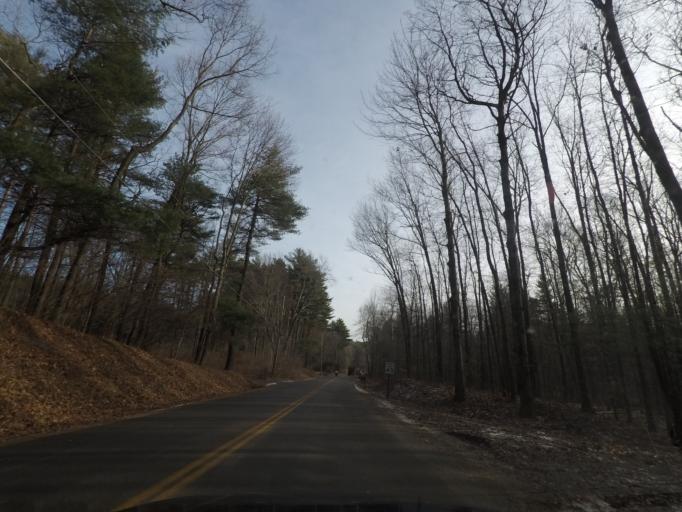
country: US
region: New York
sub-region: Saratoga County
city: Stillwater
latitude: 42.9891
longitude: -73.7189
